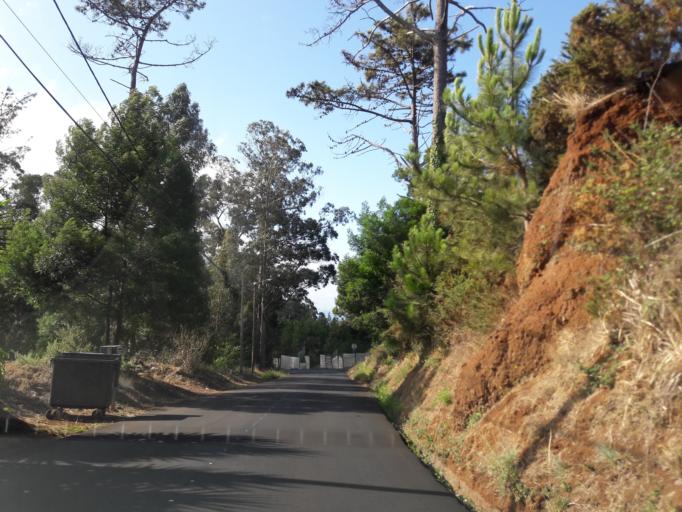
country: PT
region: Madeira
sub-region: Santa Cruz
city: Camacha
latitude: 32.6645
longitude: -16.8371
